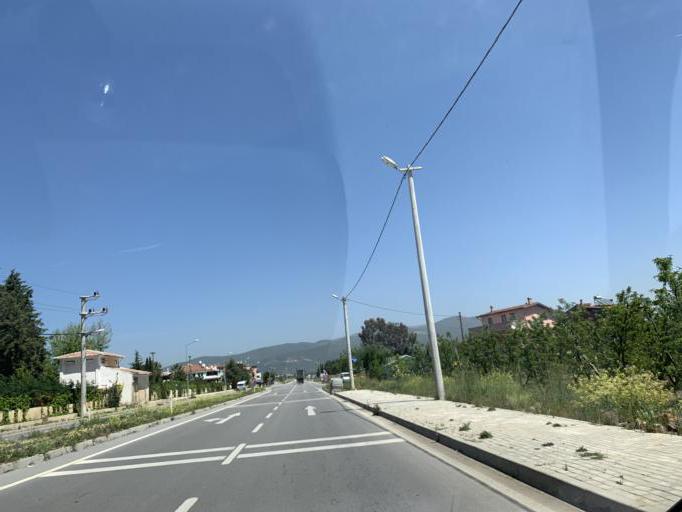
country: TR
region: Bursa
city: Iznik
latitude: 40.4089
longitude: 29.7060
